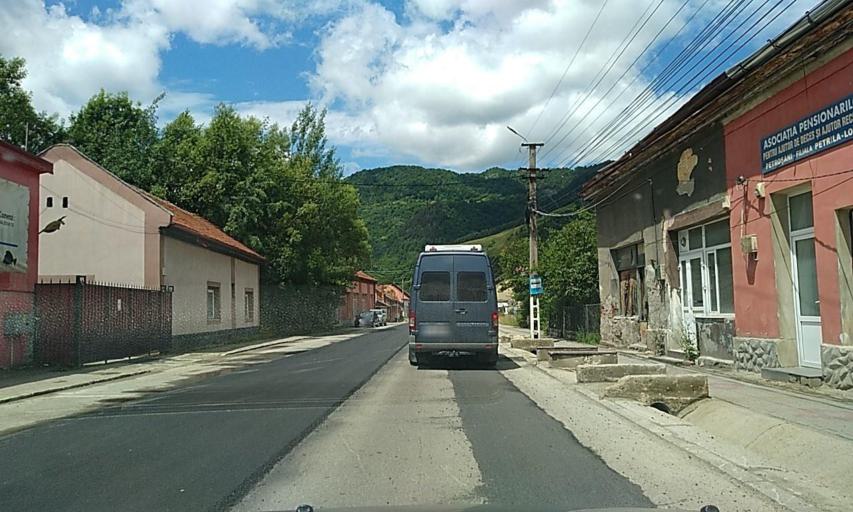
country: RO
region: Hunedoara
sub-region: Oras Petrila
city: Petrila
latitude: 45.4473
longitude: 23.4109
